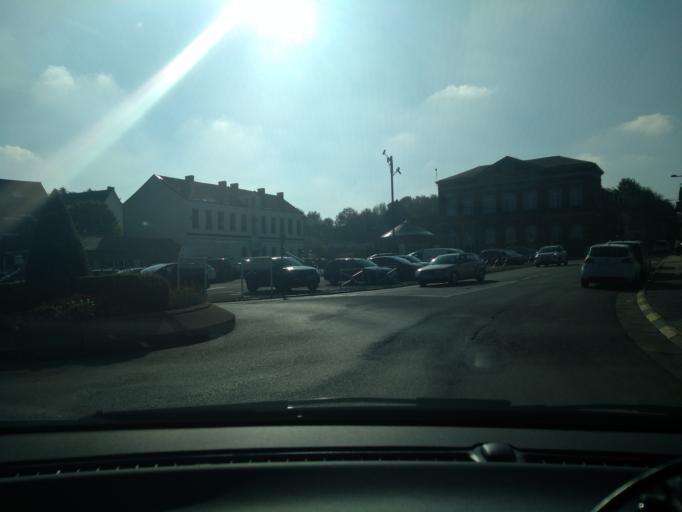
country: BE
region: Wallonia
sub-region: Province du Hainaut
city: Colfontaine
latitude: 50.4223
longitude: 3.8437
